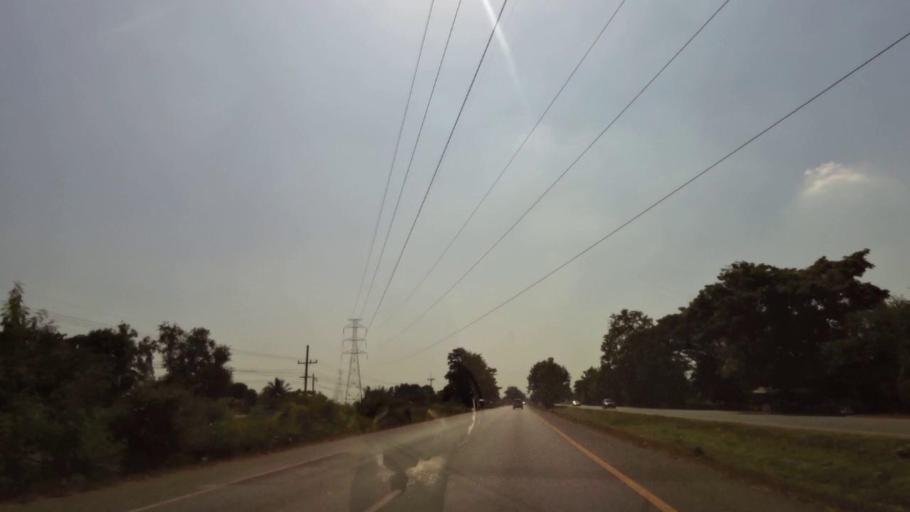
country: TH
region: Phichit
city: Wachira Barami
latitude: 16.3910
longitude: 100.1388
